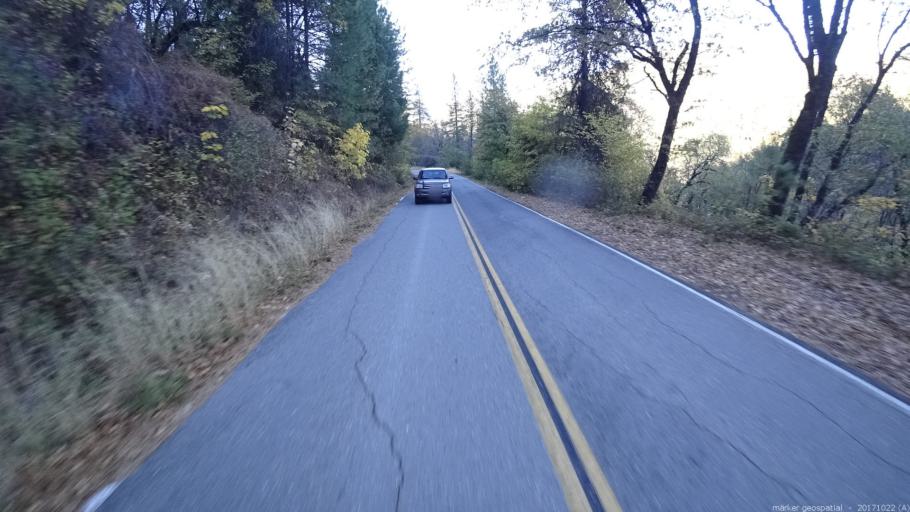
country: US
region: California
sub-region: Shasta County
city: Shasta Lake
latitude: 40.9046
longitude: -122.2357
